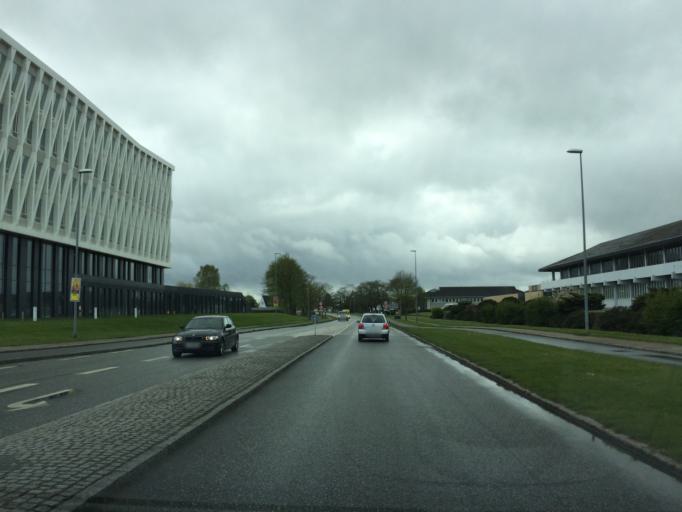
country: DK
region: Central Jutland
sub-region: Viborg Kommune
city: Viborg
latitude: 56.4596
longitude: 9.3985
